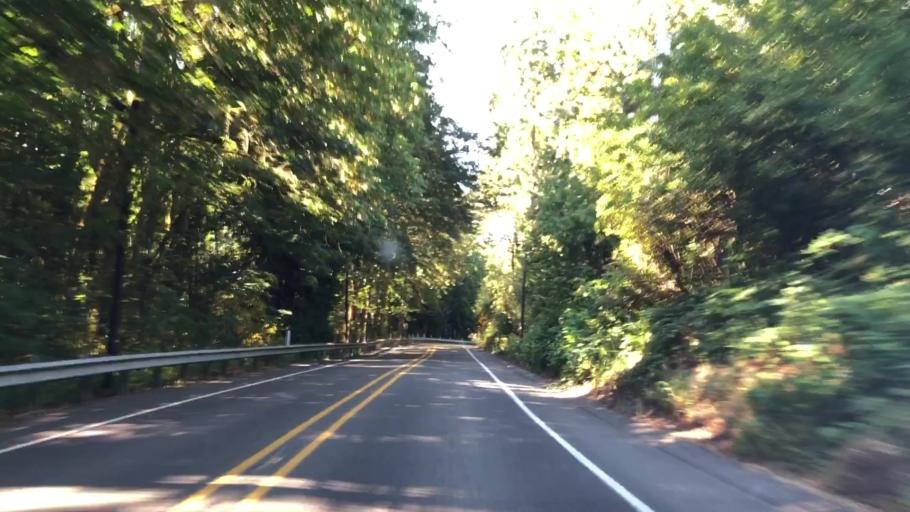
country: US
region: Washington
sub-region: Kitsap County
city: Kingston
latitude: 47.7789
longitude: -122.4996
